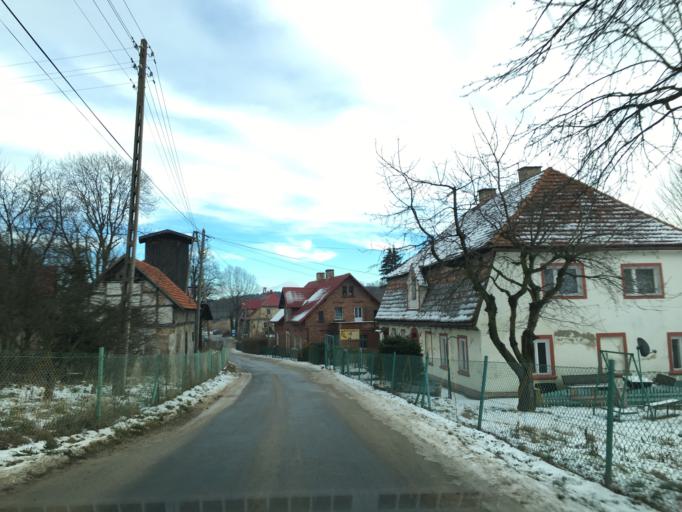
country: PL
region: Lower Silesian Voivodeship
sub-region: Powiat walbrzyski
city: Dziecmorowice
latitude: 50.7406
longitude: 16.3924
